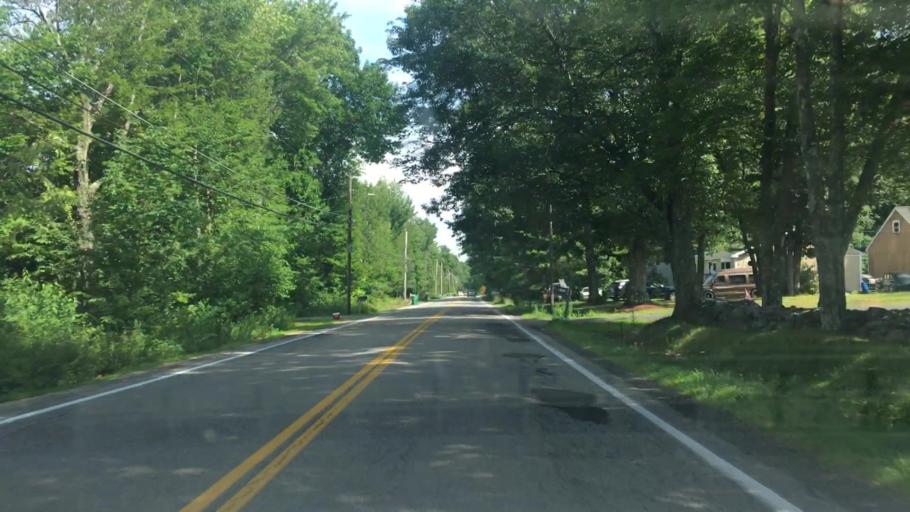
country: US
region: New Hampshire
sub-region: Strafford County
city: Rochester
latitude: 43.3160
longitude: -70.9370
